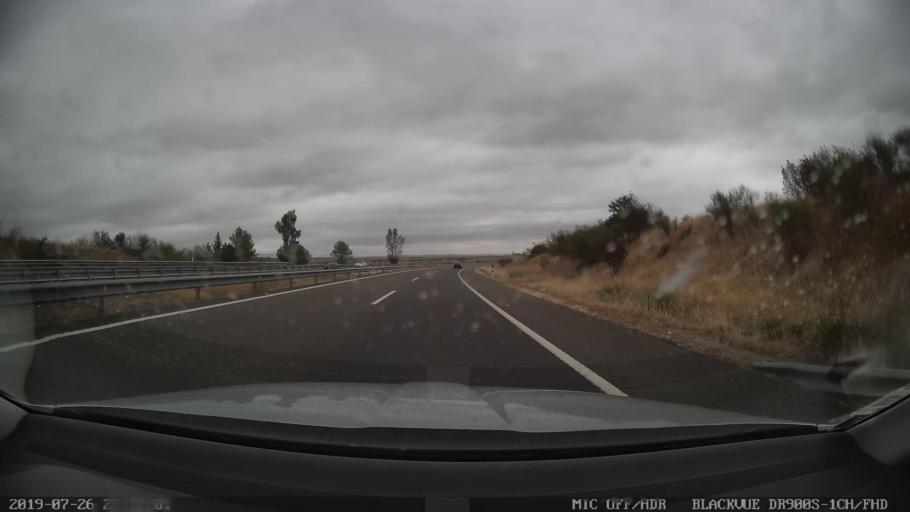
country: ES
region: Extremadura
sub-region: Provincia de Badajoz
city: Santa Amalia
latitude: 39.0638
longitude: -6.0537
